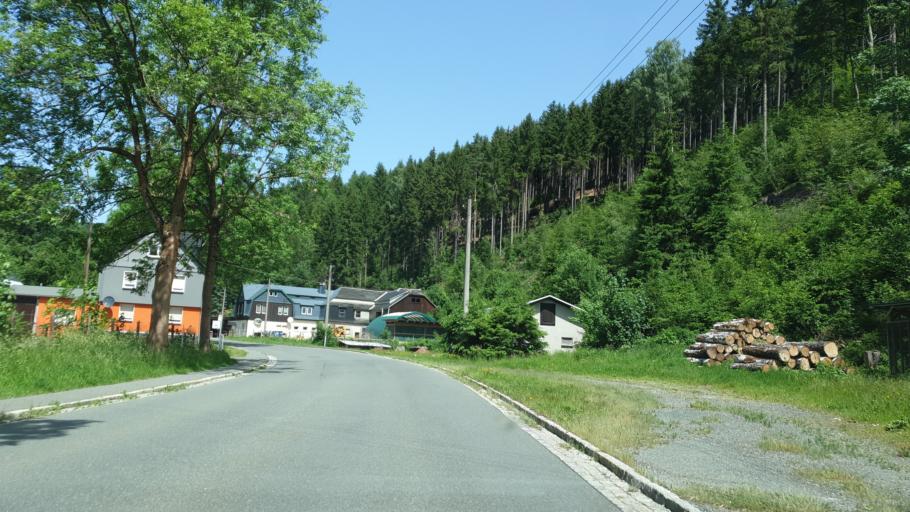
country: DE
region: Saxony
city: Klingenthal
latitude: 50.3804
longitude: 12.4620
